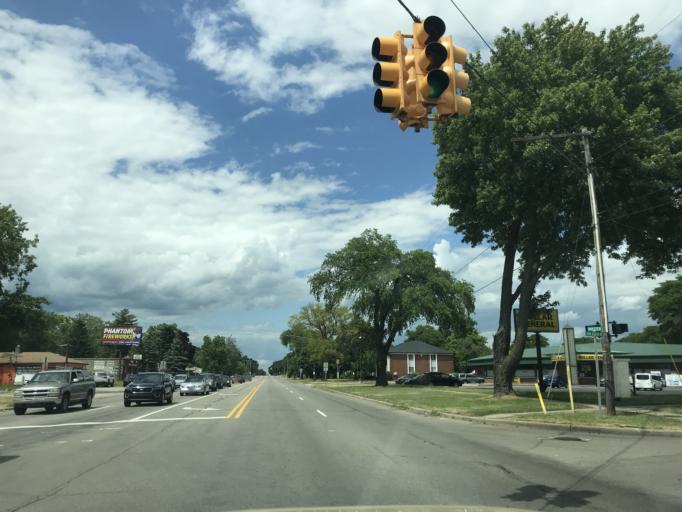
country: US
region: Michigan
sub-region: Wayne County
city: Garden City
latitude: 42.3509
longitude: -83.3126
